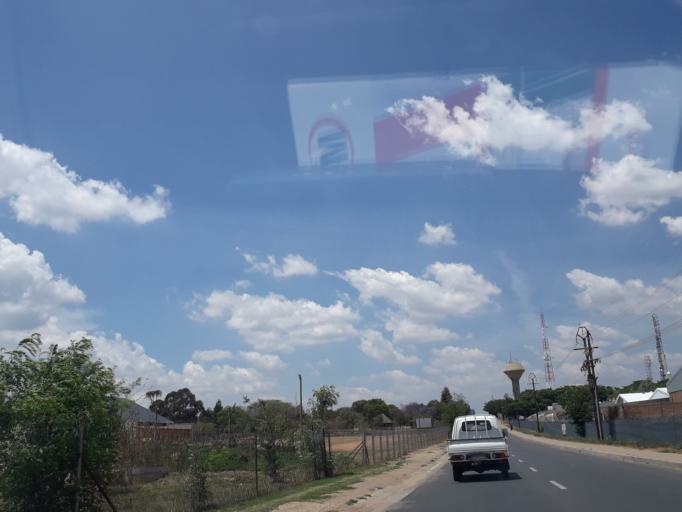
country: ZA
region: Gauteng
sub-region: West Rand District Municipality
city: Muldersdriseloop
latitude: -26.0733
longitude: 27.9244
